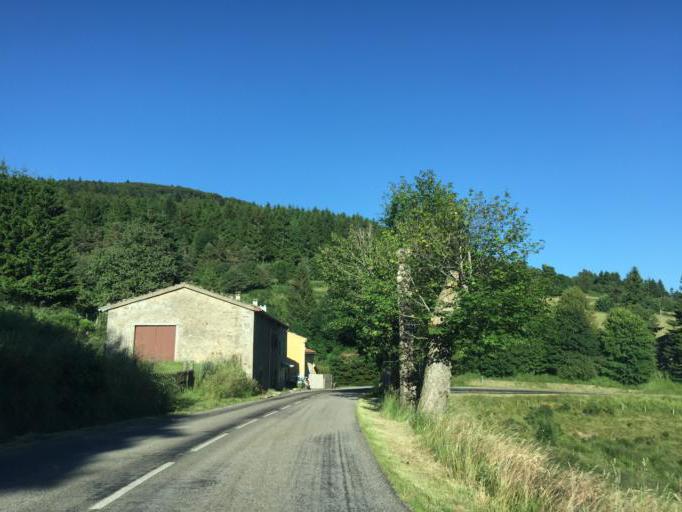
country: FR
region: Rhone-Alpes
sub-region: Departement de la Loire
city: Bourg-Argental
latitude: 45.3663
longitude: 4.5405
